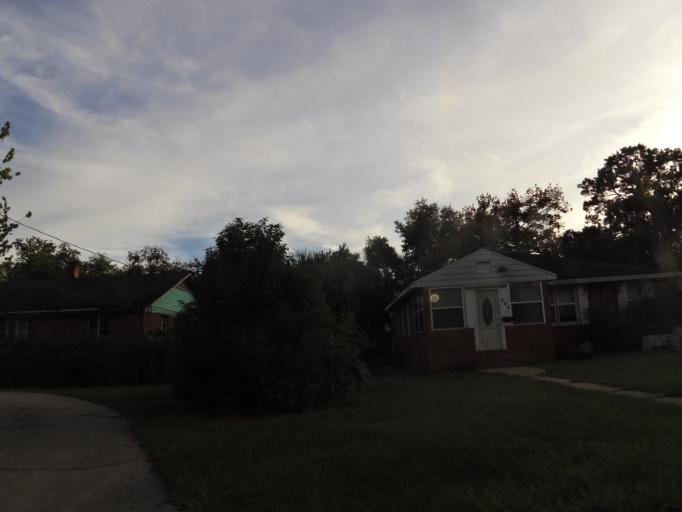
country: US
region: Florida
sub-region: Duval County
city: Jacksonville
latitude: 30.3878
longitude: -81.6582
